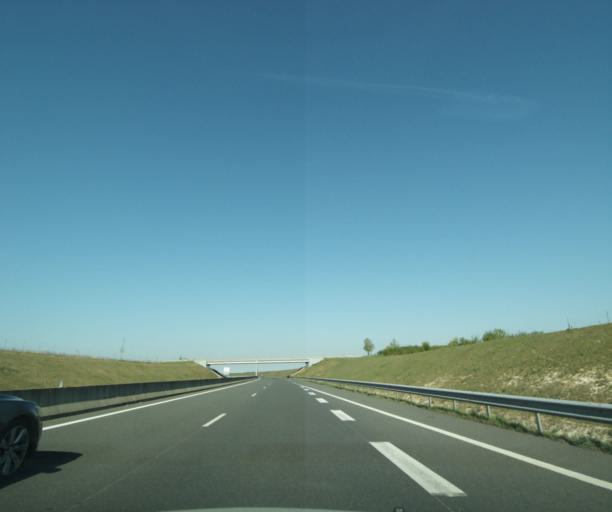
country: FR
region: Centre
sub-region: Departement du Loiret
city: Puiseaux
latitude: 48.0976
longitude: 2.0664
